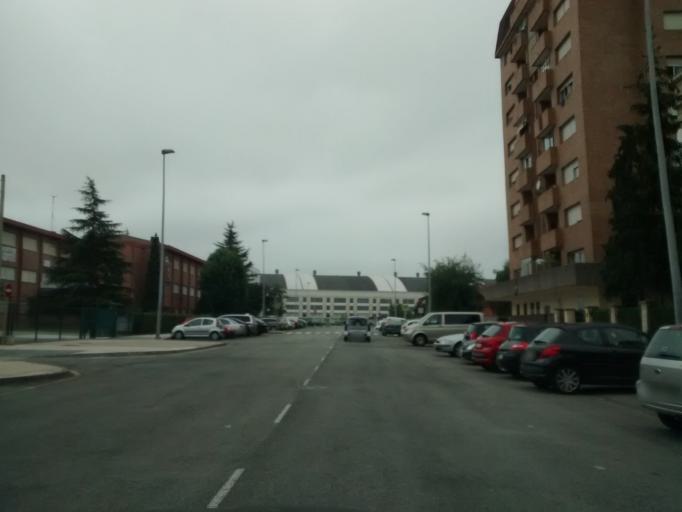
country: ES
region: Cantabria
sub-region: Provincia de Cantabria
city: Torrelavega
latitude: 43.3457
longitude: -4.0488
